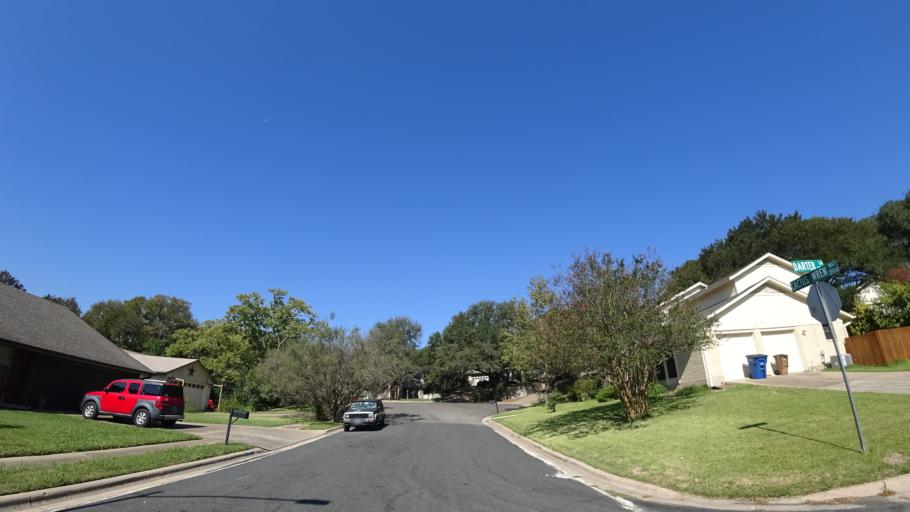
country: US
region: Texas
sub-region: Travis County
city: Rollingwood
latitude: 30.2715
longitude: -97.8075
